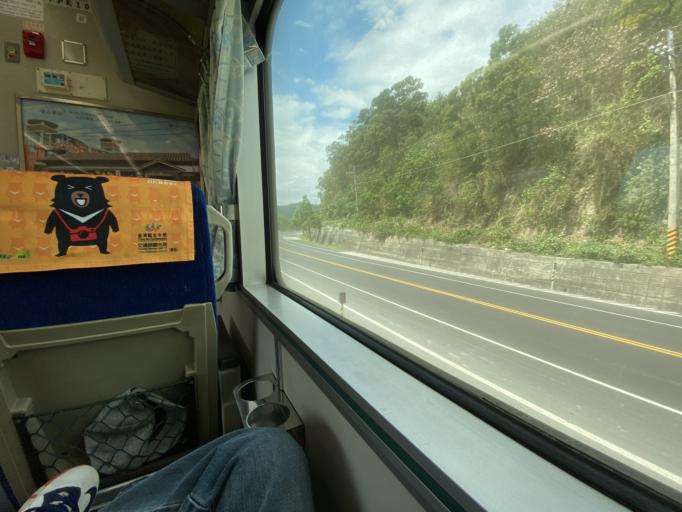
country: TW
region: Taiwan
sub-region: Taitung
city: Taitung
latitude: 22.9028
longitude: 121.1379
